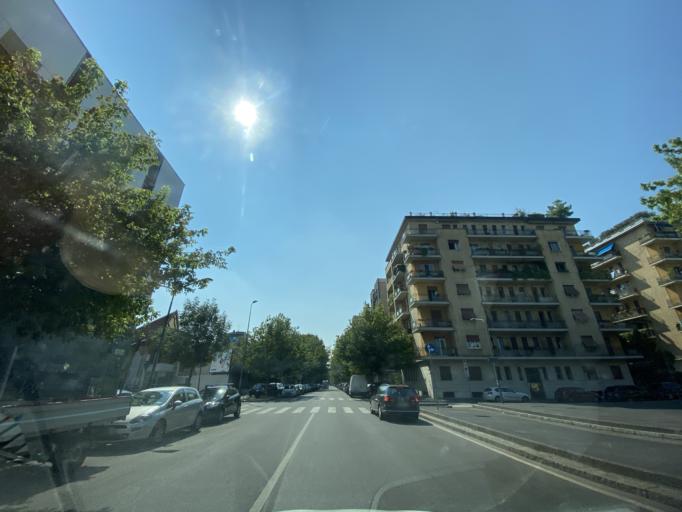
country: IT
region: Lombardy
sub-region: Citta metropolitana di Milano
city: Milano
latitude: 45.4819
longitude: 9.1594
